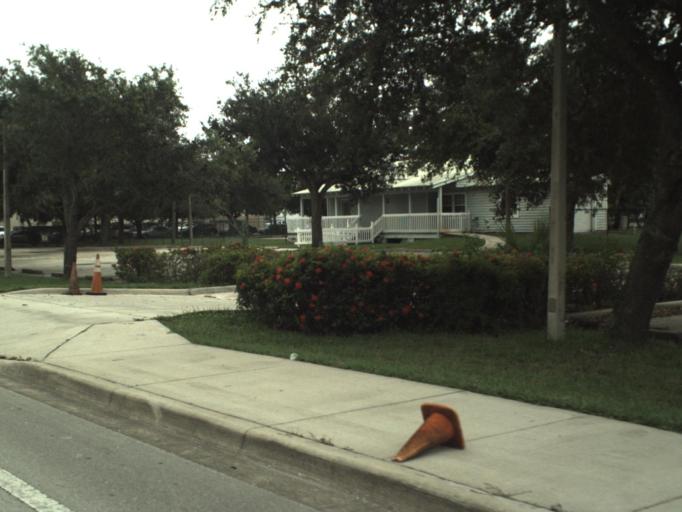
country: US
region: Florida
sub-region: Palm Beach County
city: Mangonia Park
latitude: 26.7680
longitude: -80.1078
